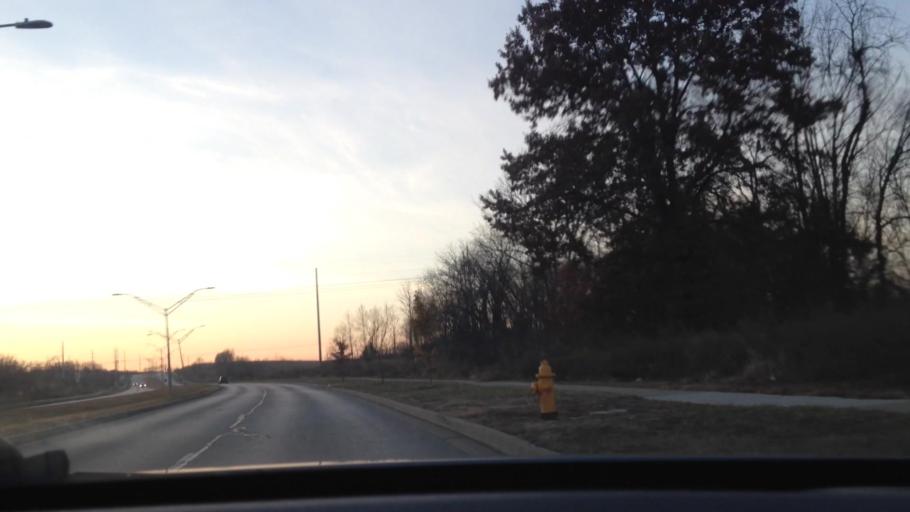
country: US
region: Missouri
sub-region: Clay County
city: Pleasant Valley
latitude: 39.2103
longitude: -94.4545
